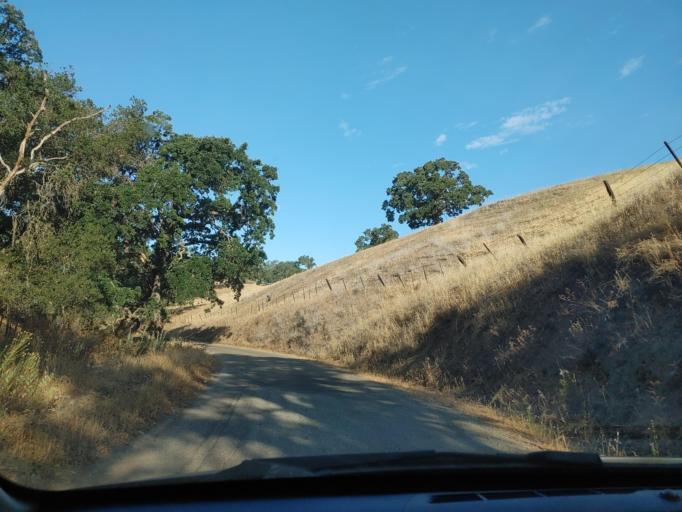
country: US
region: California
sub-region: San Benito County
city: Ridgemark
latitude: 36.7702
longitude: -121.2036
